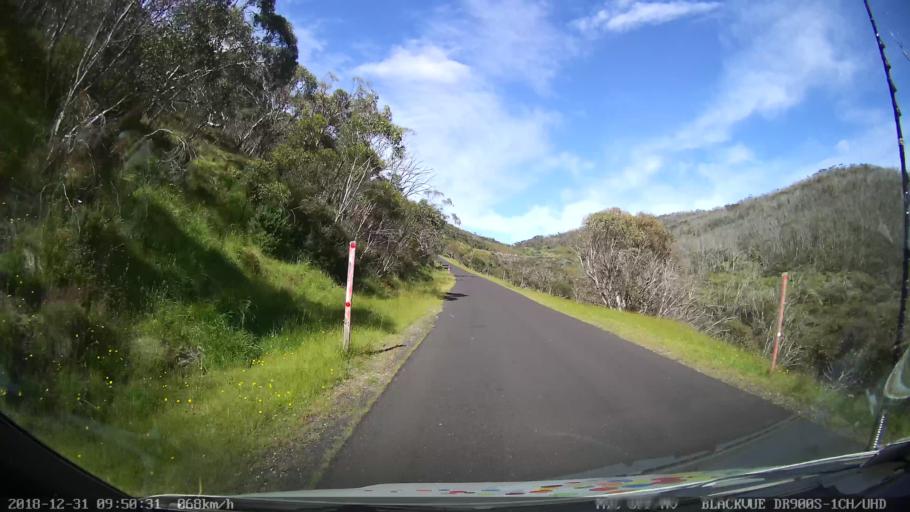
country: AU
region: New South Wales
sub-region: Snowy River
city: Jindabyne
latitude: -36.5206
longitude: 148.2721
